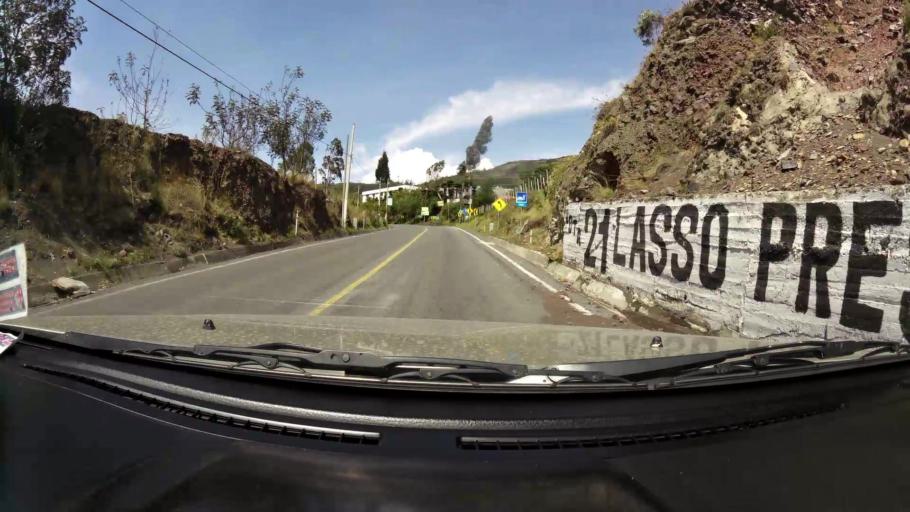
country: EC
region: Chimborazo
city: Guano
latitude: -1.5665
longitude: -78.5337
